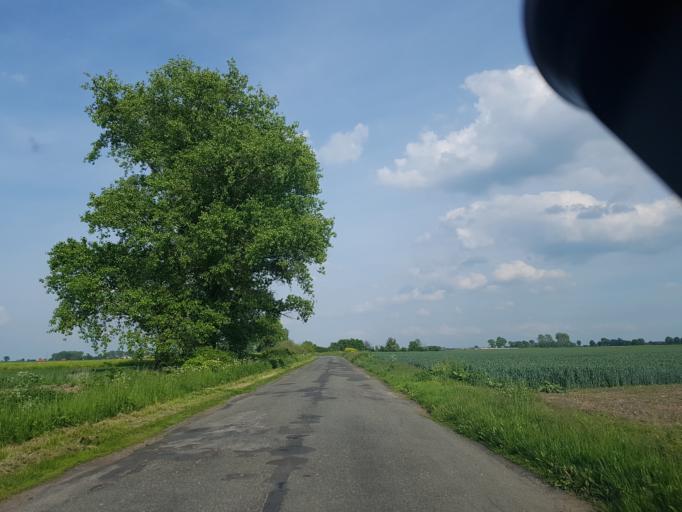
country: PL
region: Lower Silesian Voivodeship
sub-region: Powiat strzelinski
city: Wiazow
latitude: 50.8653
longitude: 17.1644
